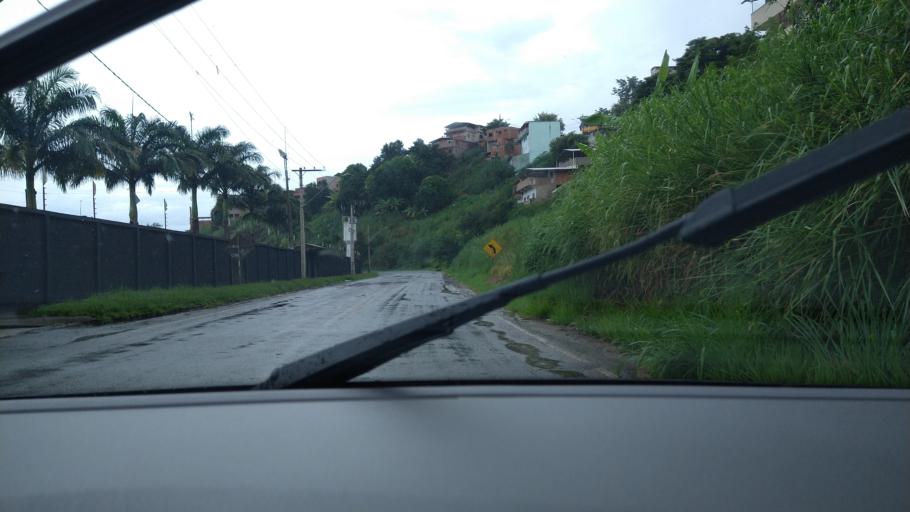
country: BR
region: Minas Gerais
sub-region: Ponte Nova
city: Ponte Nova
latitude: -20.3972
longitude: -42.9008
